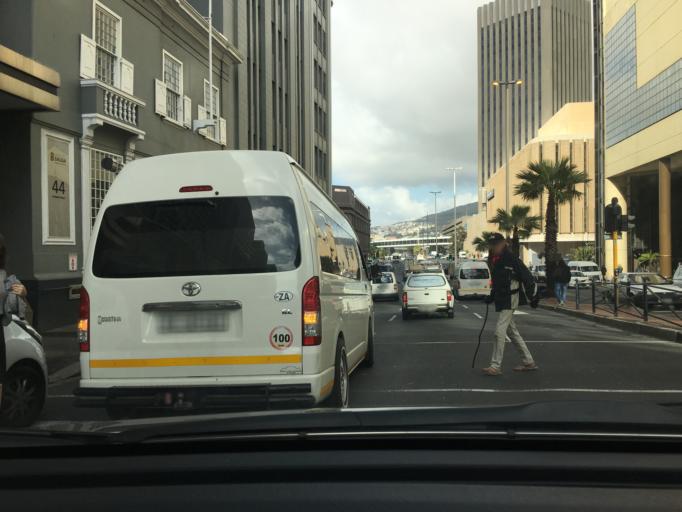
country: ZA
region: Western Cape
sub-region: City of Cape Town
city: Cape Town
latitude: -33.9210
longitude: 18.4218
